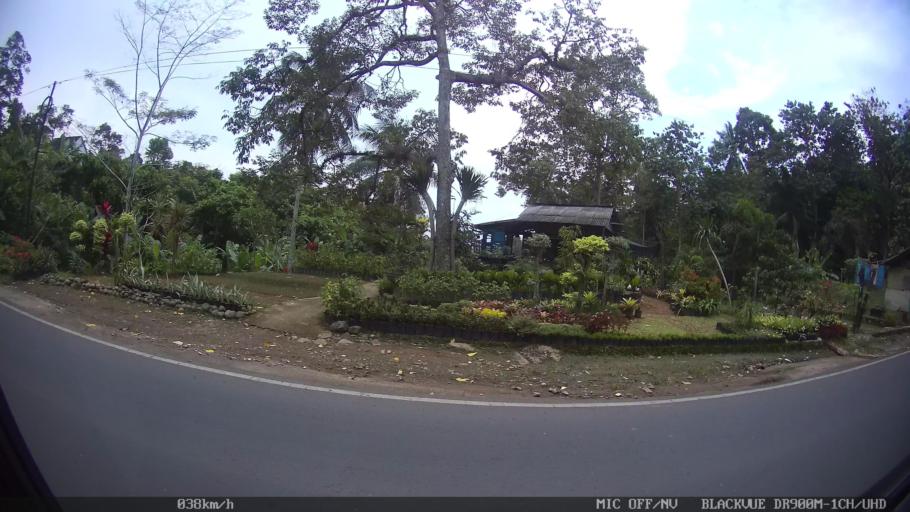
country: ID
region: Lampung
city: Bandarlampung
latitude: -5.4121
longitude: 105.2259
